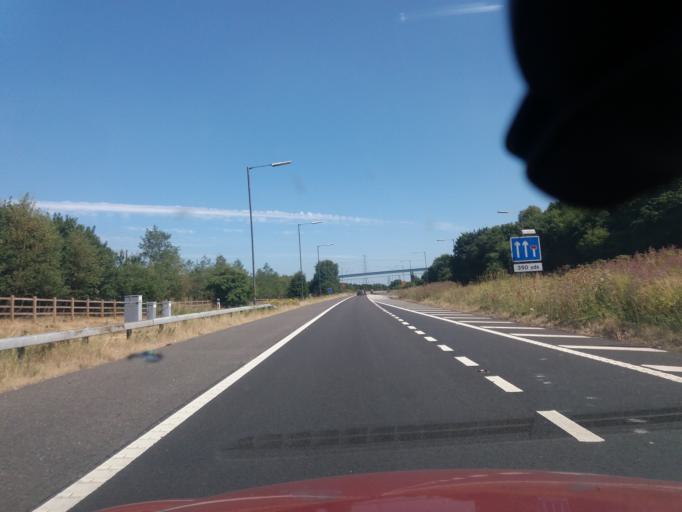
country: GB
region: England
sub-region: Borough of Bolton
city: Kearsley
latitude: 53.5318
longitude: -2.3780
